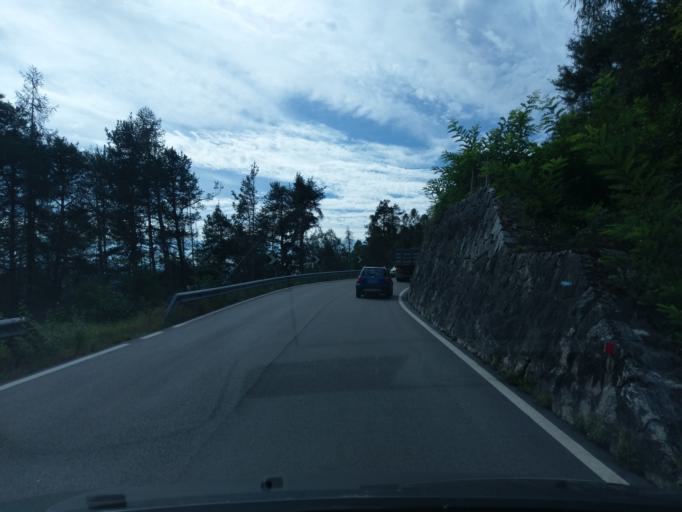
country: IT
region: Trentino-Alto Adige
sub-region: Provincia di Trento
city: Cagno
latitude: 46.3846
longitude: 11.0380
